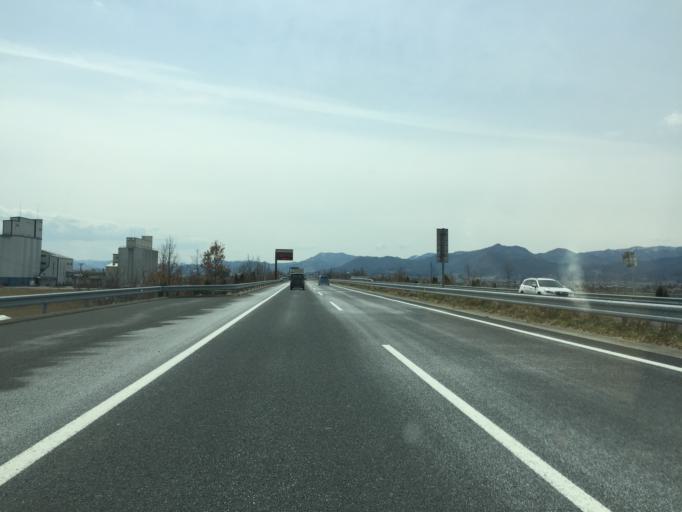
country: JP
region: Yamagata
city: Yamagata-shi
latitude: 38.2763
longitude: 140.2958
